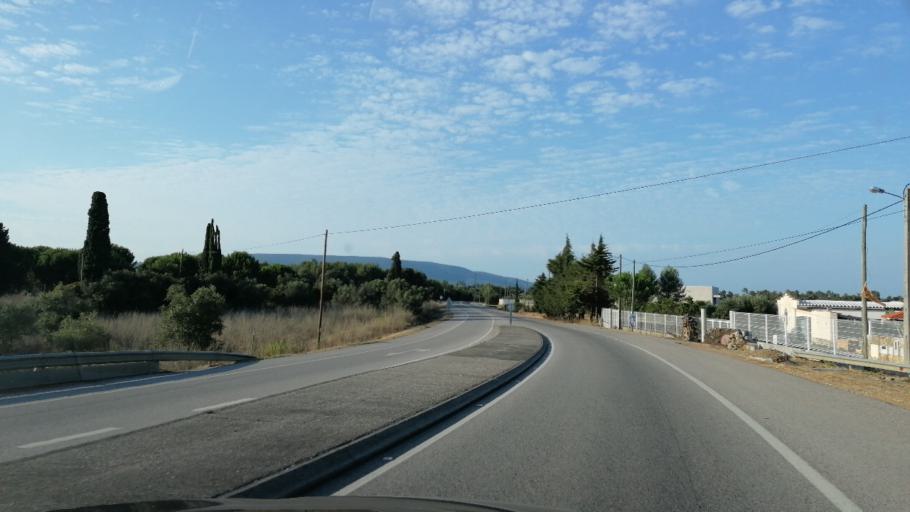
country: PT
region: Santarem
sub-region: Alcanena
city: Alcanena
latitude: 39.4362
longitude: -8.6260
